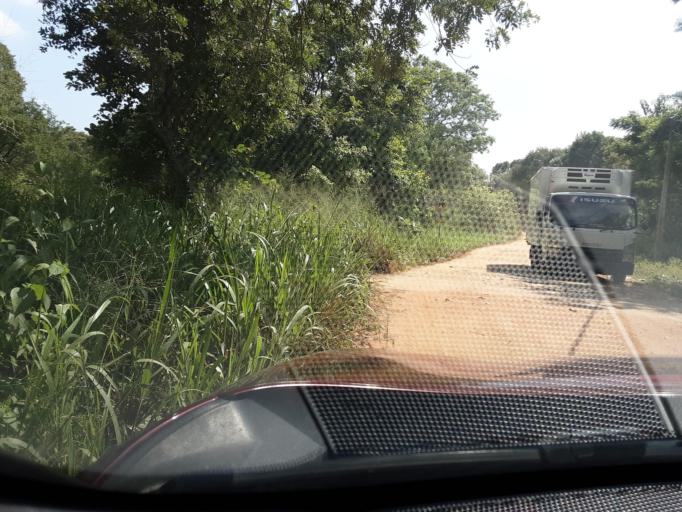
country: LK
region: Central
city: Sigiriya
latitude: 8.0036
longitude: 80.7470
